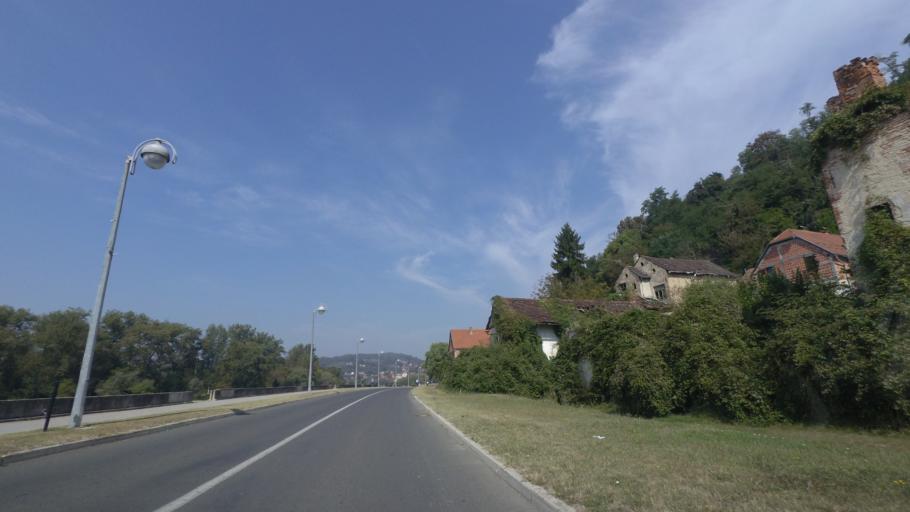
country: BA
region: Republika Srpska
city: Kostajnica
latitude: 45.2231
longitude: 16.5473
